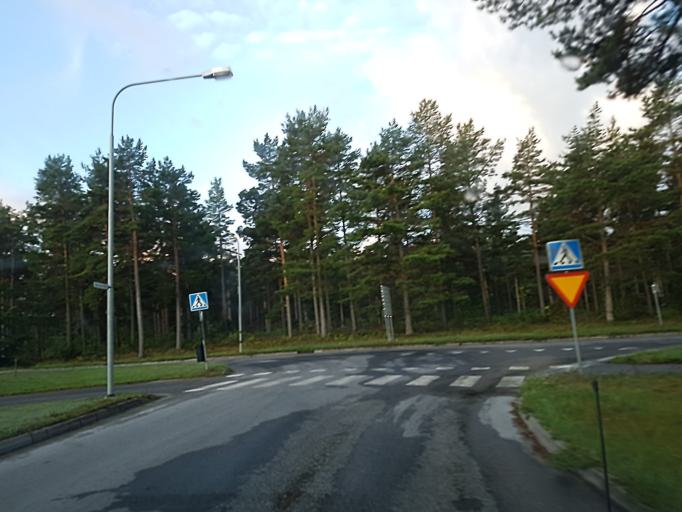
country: SE
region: Gotland
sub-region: Gotland
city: Visby
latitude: 57.6078
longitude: 18.3009
